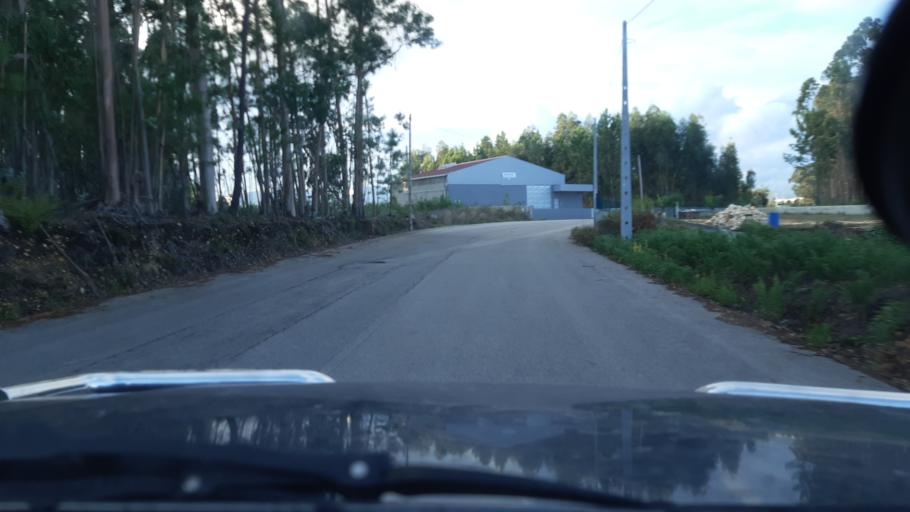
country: PT
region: Aveiro
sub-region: Agueda
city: Agueda
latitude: 40.5787
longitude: -8.4695
